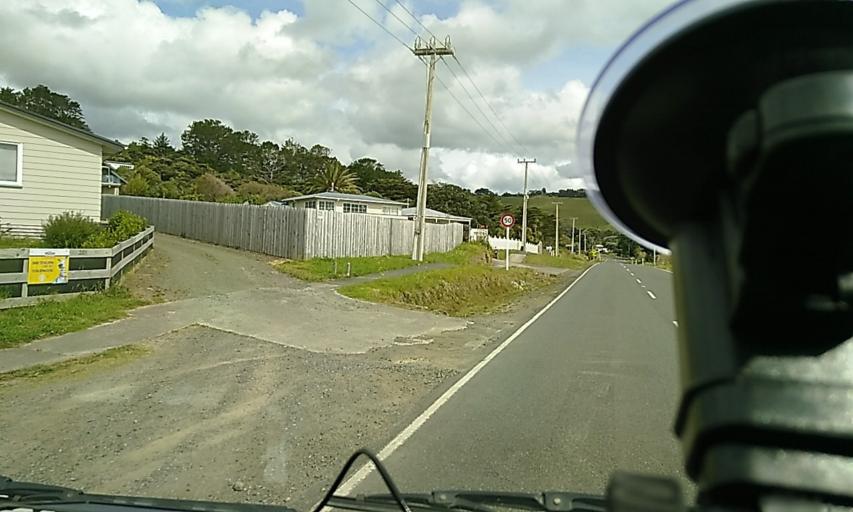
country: NZ
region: Northland
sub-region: Far North District
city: Ahipara
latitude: -35.5224
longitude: 173.3890
